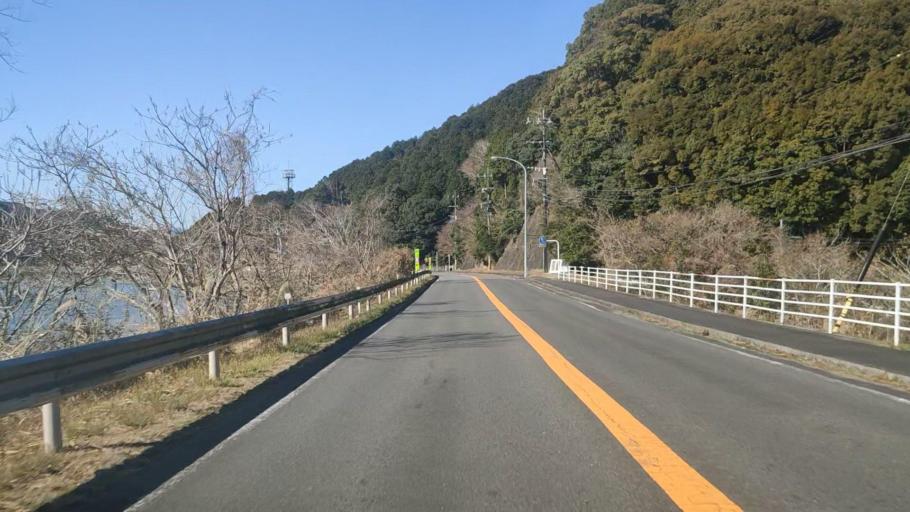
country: JP
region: Oita
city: Saiki
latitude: 32.9407
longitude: 131.9130
